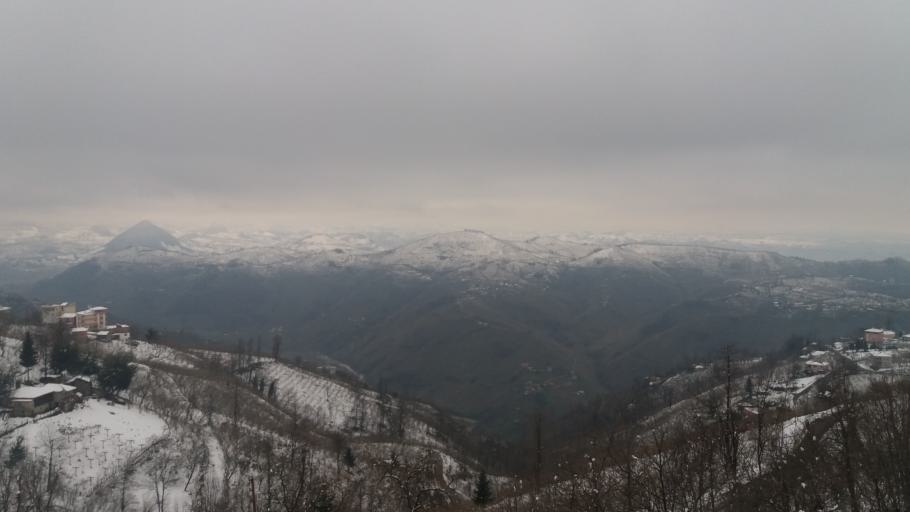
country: TR
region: Ordu
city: Kabaduz
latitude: 40.8597
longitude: 37.8902
